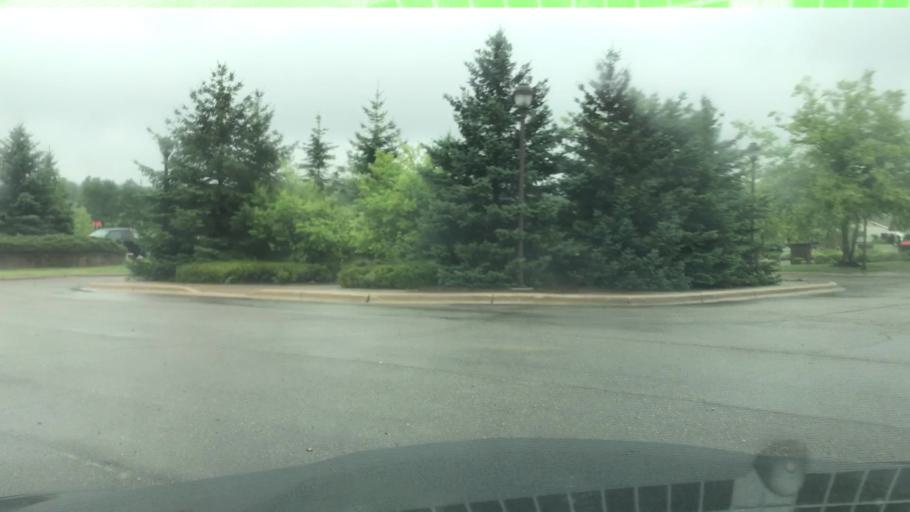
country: US
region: Michigan
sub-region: Oakland County
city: Auburn Hills
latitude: 42.7267
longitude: -83.3061
